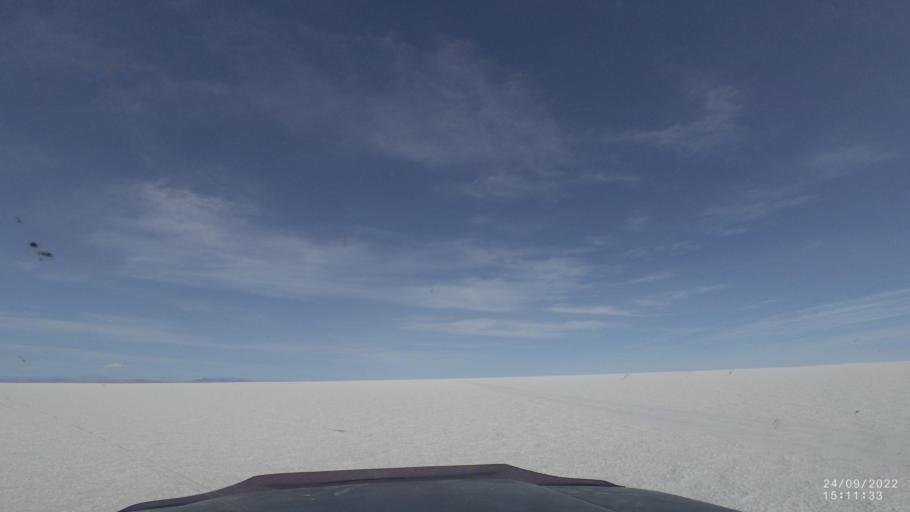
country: BO
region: Potosi
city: Colchani
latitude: -19.9454
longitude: -67.4762
